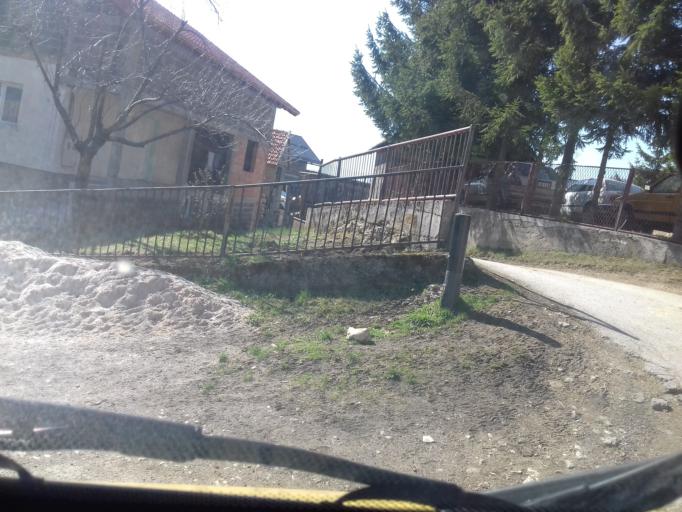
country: BA
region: Federation of Bosnia and Herzegovina
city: Travnik
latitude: 44.2430
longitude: 17.7191
